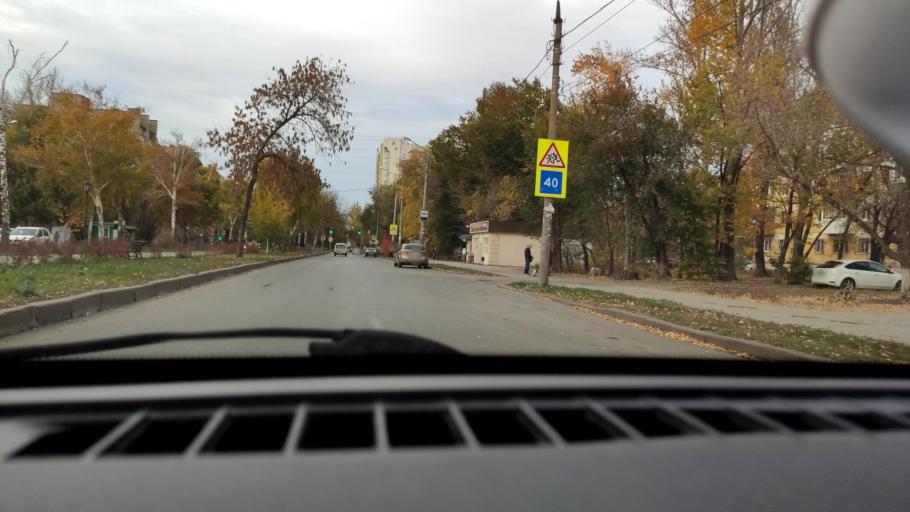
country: RU
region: Samara
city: Samara
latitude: 53.1951
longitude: 50.1790
